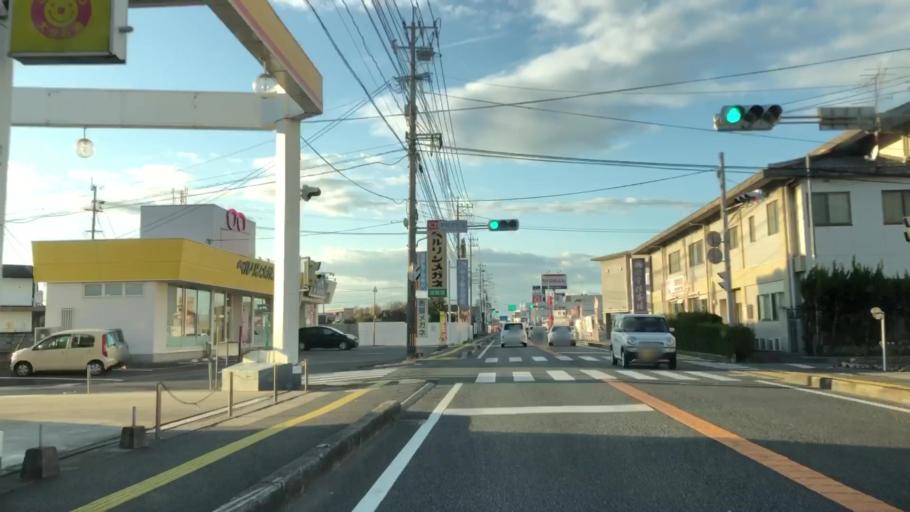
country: JP
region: Oita
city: Bungo-Takada-shi
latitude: 33.5322
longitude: 131.3329
